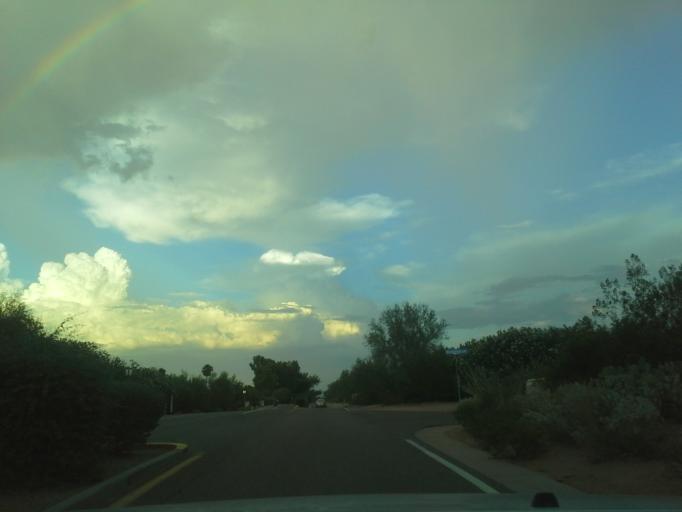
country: US
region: Arizona
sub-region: Maricopa County
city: Paradise Valley
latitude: 33.5238
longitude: -111.9568
